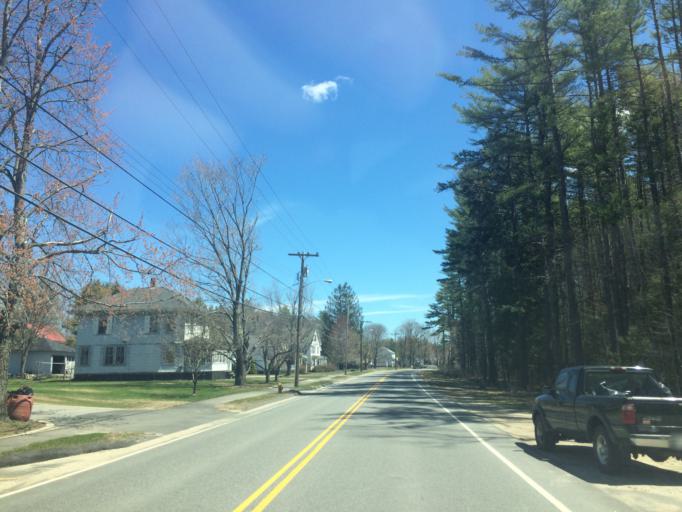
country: US
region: Maine
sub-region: Oxford County
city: Porter
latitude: 43.8067
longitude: -70.8803
